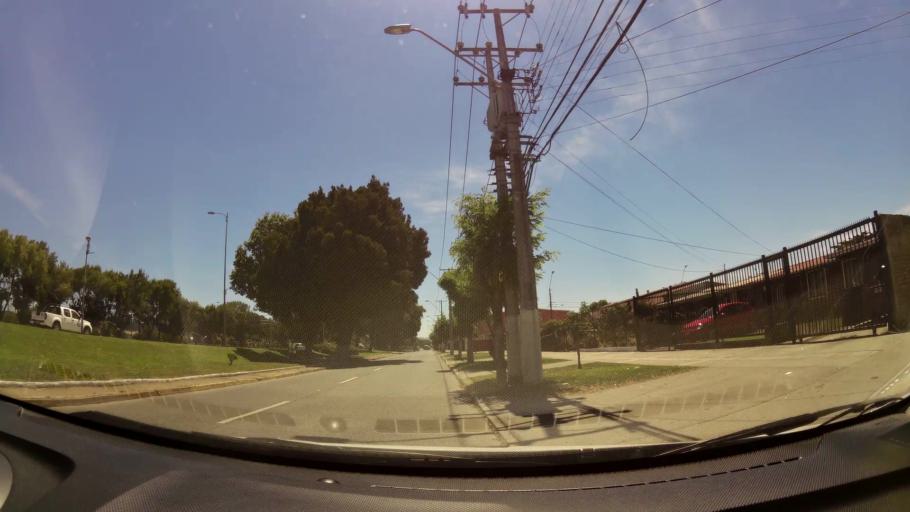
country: CL
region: Biobio
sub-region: Provincia de Concepcion
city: Talcahuano
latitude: -36.7631
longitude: -73.0871
